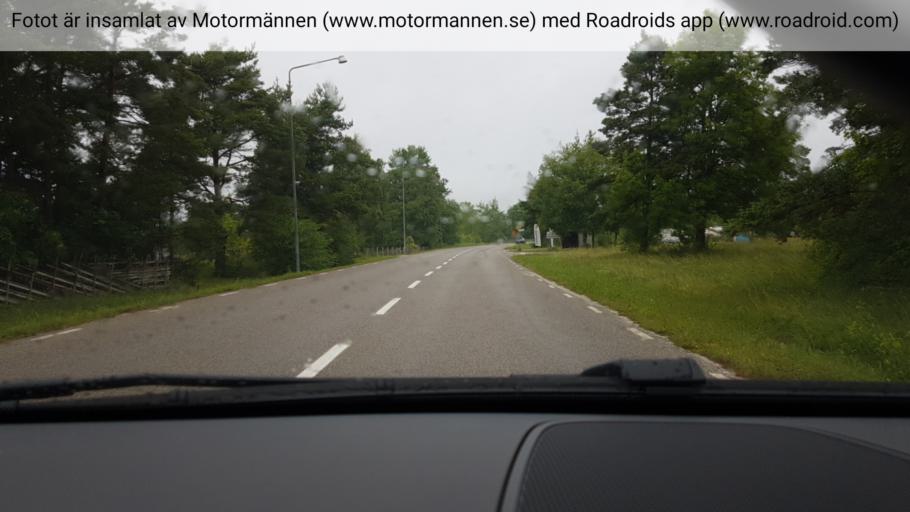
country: SE
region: Gotland
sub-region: Gotland
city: Slite
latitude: 57.8442
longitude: 18.7806
